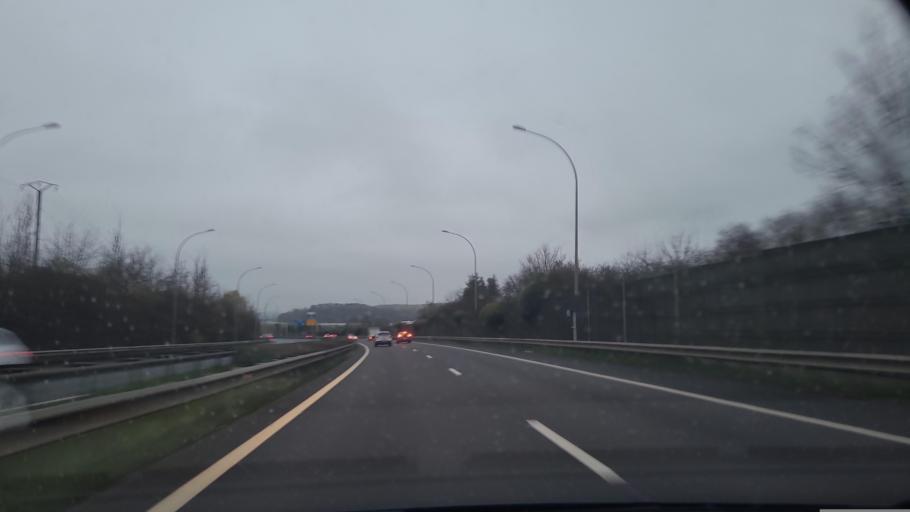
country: LU
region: Luxembourg
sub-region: Canton d'Esch-sur-Alzette
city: Schifflange
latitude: 49.5276
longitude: 6.0098
